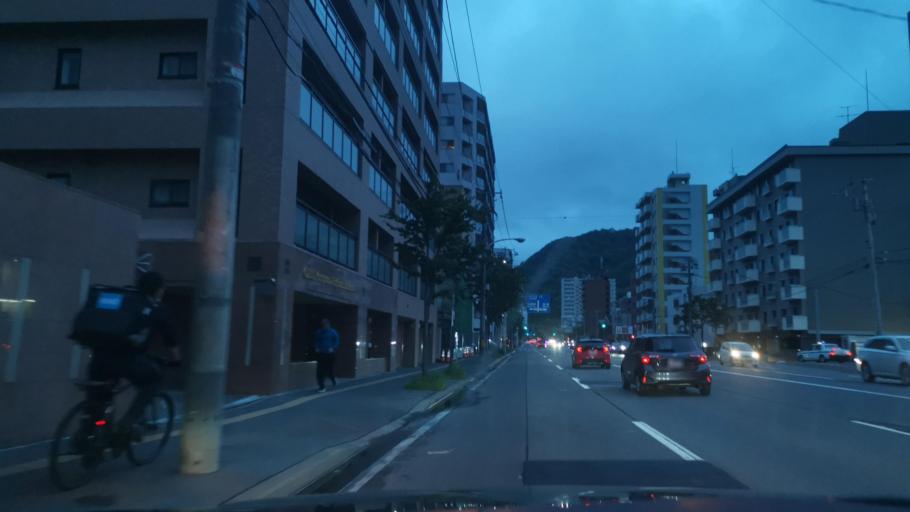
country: JP
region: Hokkaido
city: Sapporo
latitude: 43.0593
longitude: 141.3151
